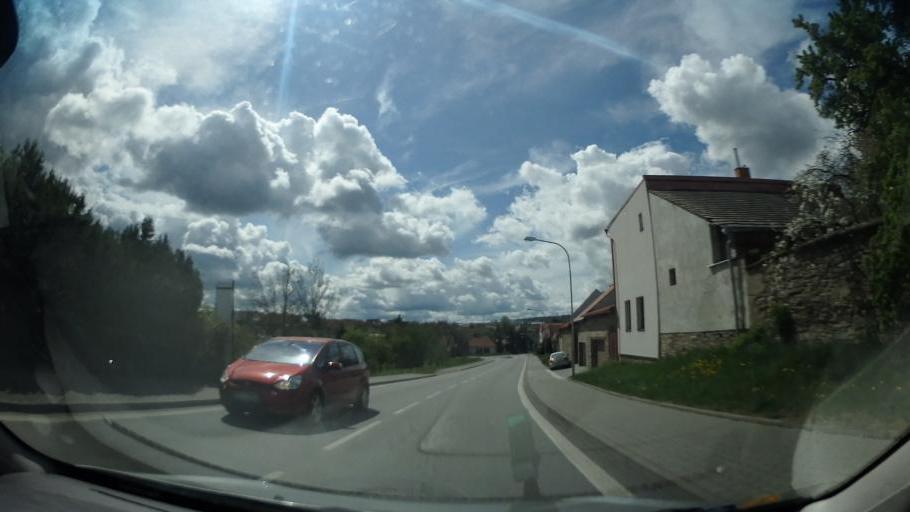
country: CZ
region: Vysocina
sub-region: Okres Zd'ar nad Sazavou
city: Velka Bites
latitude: 49.2896
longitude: 16.2288
